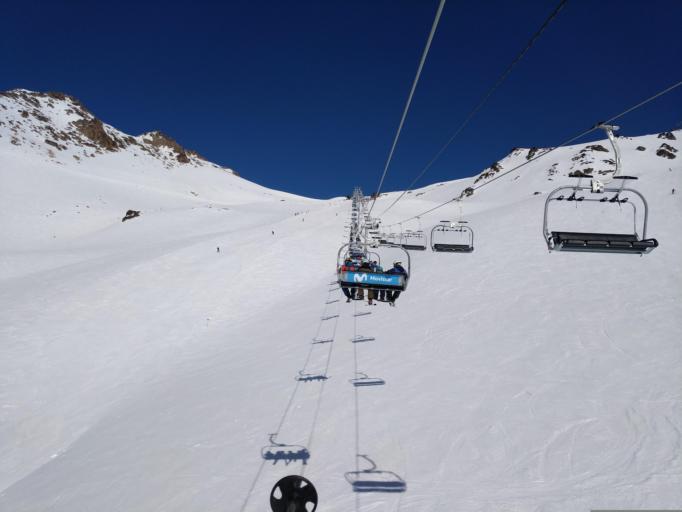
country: AR
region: Rio Negro
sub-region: Departamento de Bariloche
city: San Carlos de Bariloche
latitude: -41.1696
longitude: -71.4766
